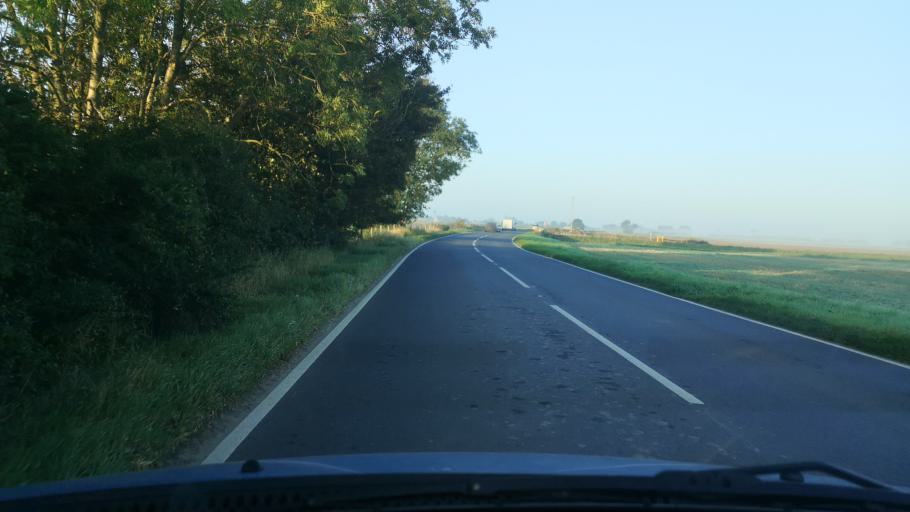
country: GB
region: England
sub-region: North Lincolnshire
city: Crowle
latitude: 53.6190
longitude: -0.8128
